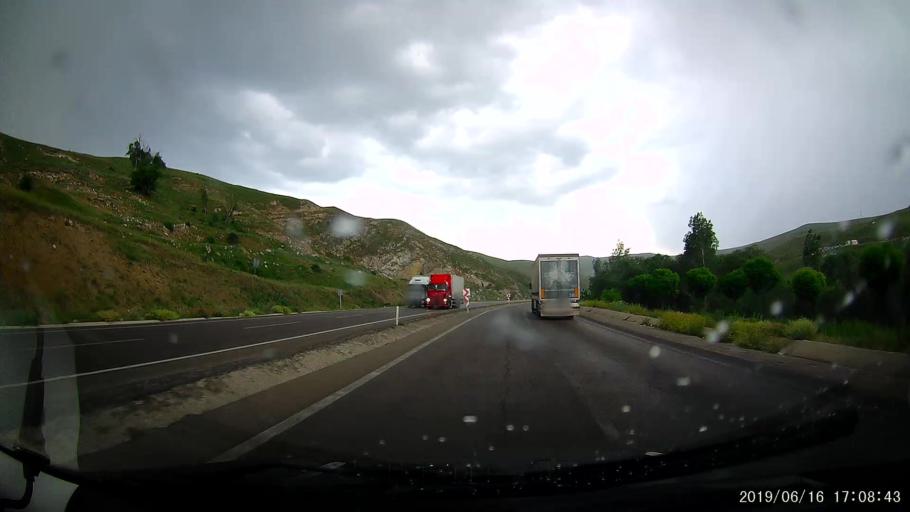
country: TR
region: Erzurum
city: Askale
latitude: 39.9044
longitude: 40.6587
